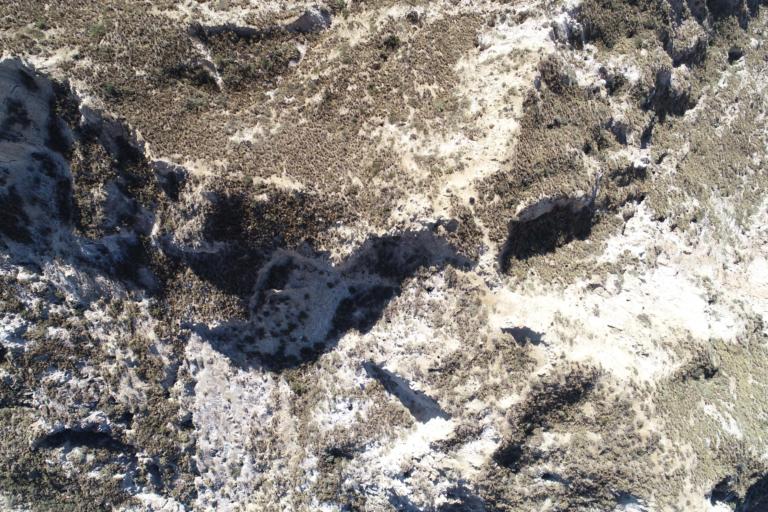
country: BO
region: La Paz
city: La Paz
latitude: -16.5518
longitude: -68.1094
